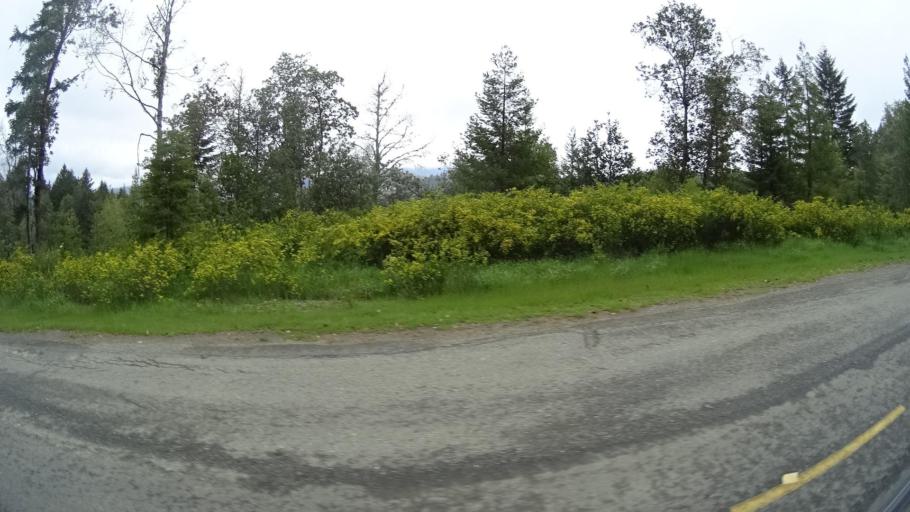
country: US
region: California
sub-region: Humboldt County
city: Redway
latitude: 40.2746
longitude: -123.7846
